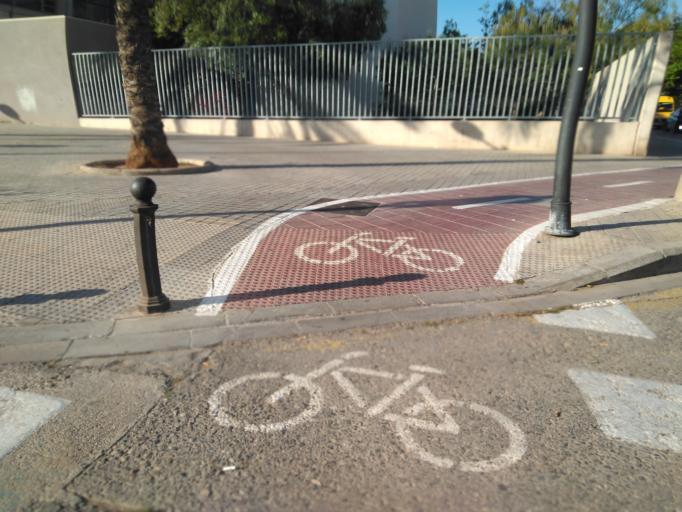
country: ES
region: Valencia
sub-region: Provincia de Valencia
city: Tavernes Blanques
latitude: 39.4928
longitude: -0.3681
